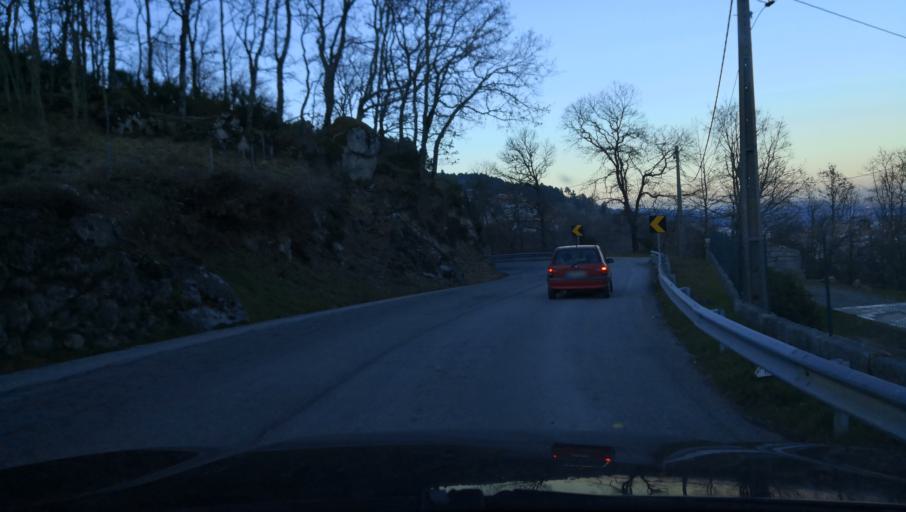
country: PT
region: Vila Real
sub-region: Vila Pouca de Aguiar
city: Vila Pouca de Aguiar
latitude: 41.4914
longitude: -7.6540
